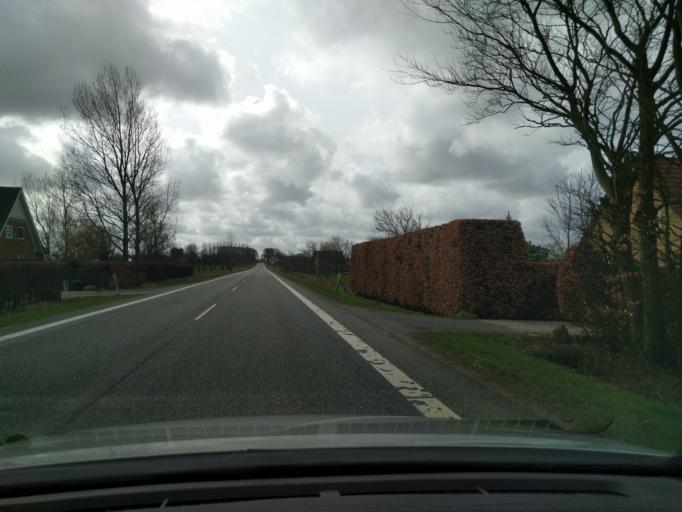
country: DK
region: South Denmark
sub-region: Tonder Kommune
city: Toftlund
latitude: 55.1440
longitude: 9.0152
